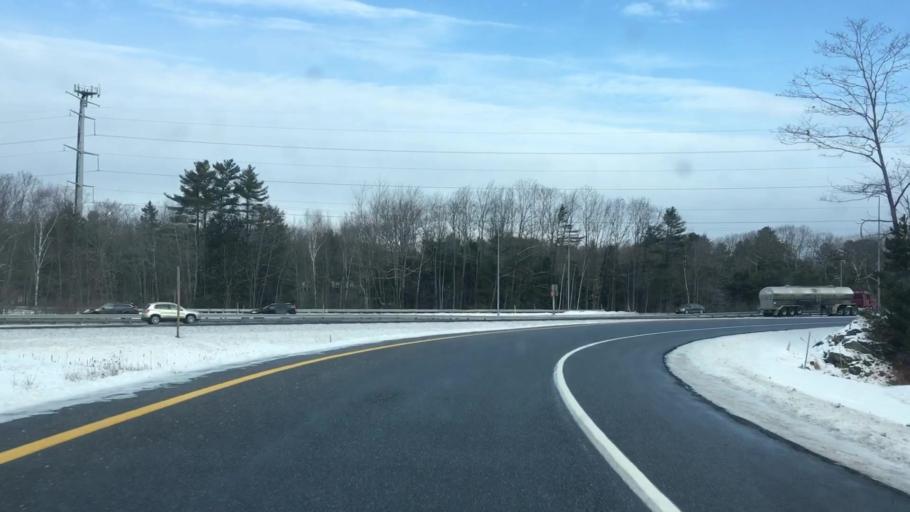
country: US
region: Maine
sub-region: Cumberland County
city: Yarmouth
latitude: 43.7852
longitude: -70.1882
